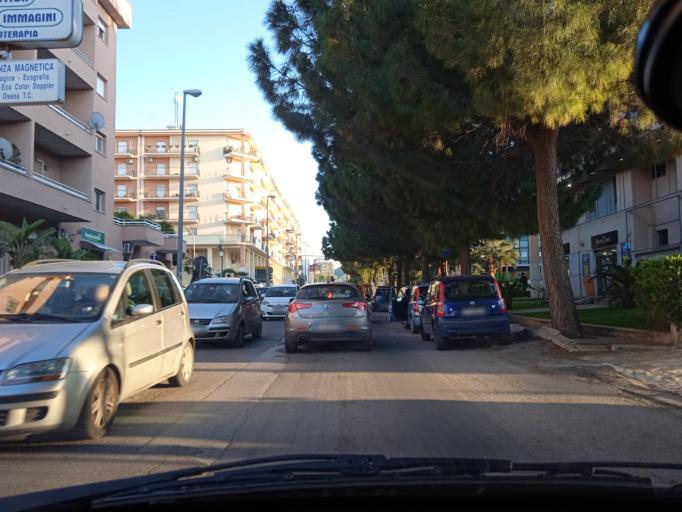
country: IT
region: Sicily
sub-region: Palermo
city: Bagheria
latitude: 38.0845
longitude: 13.5013
